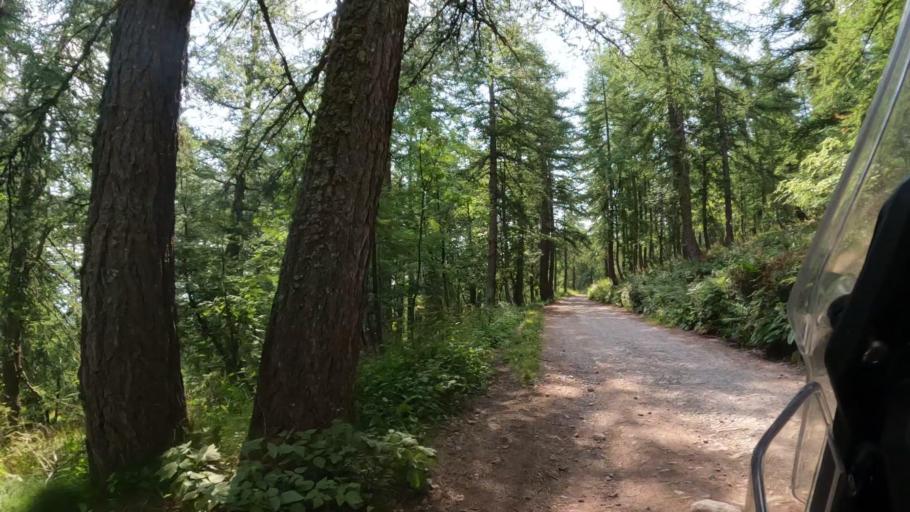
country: IT
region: Piedmont
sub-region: Provincia di Cuneo
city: Briga Alta
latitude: 44.1200
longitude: 7.6968
